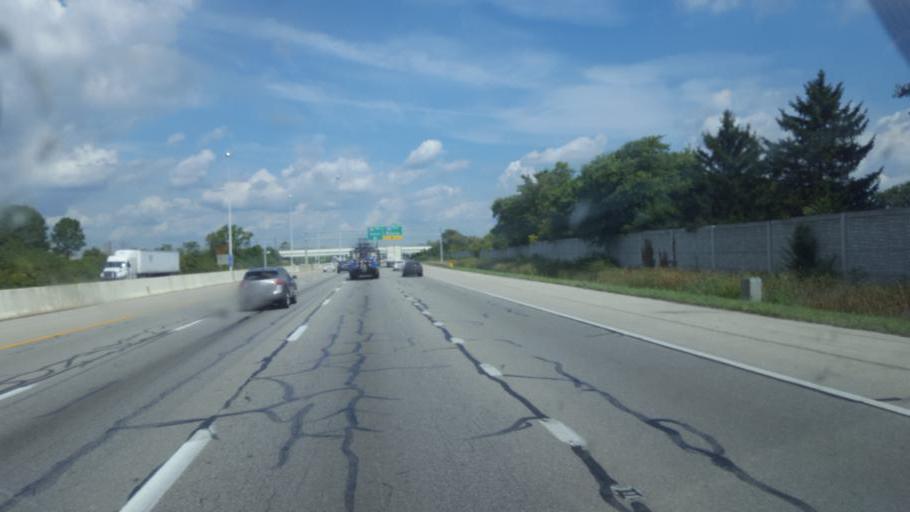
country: US
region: Ohio
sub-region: Franklin County
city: Worthington
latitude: 40.1024
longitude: -82.9829
